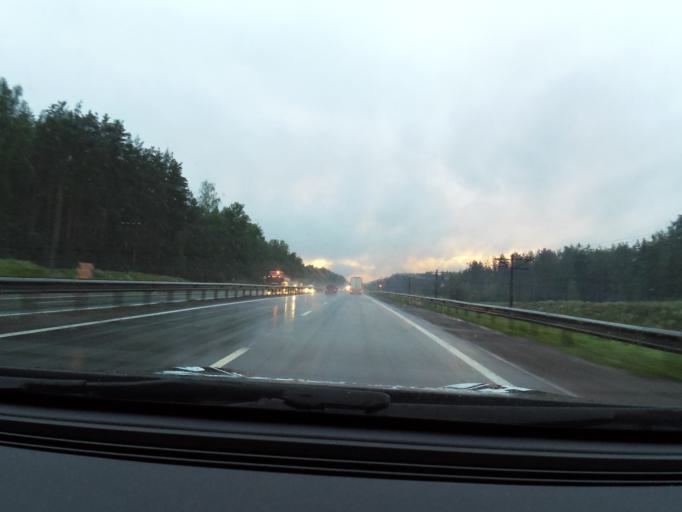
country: RU
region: Tatarstan
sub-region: Tukayevskiy Rayon
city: Naberezhnyye Chelny
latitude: 55.7280
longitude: 52.2564
